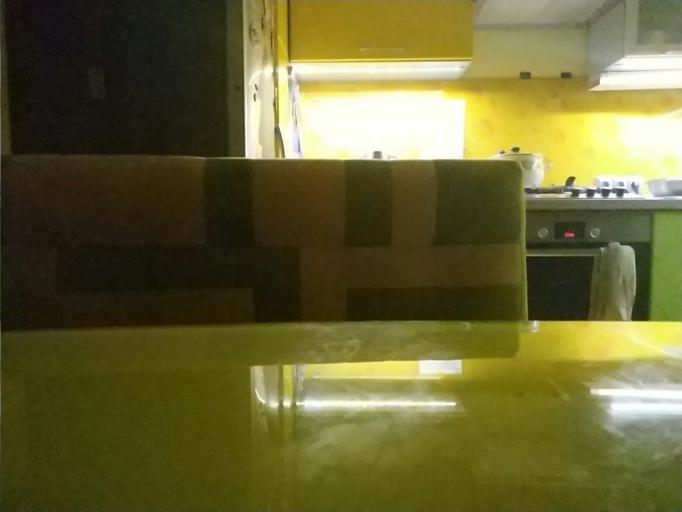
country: RU
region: Republic of Karelia
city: Pyaozerskiy
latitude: 65.7450
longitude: 30.4982
